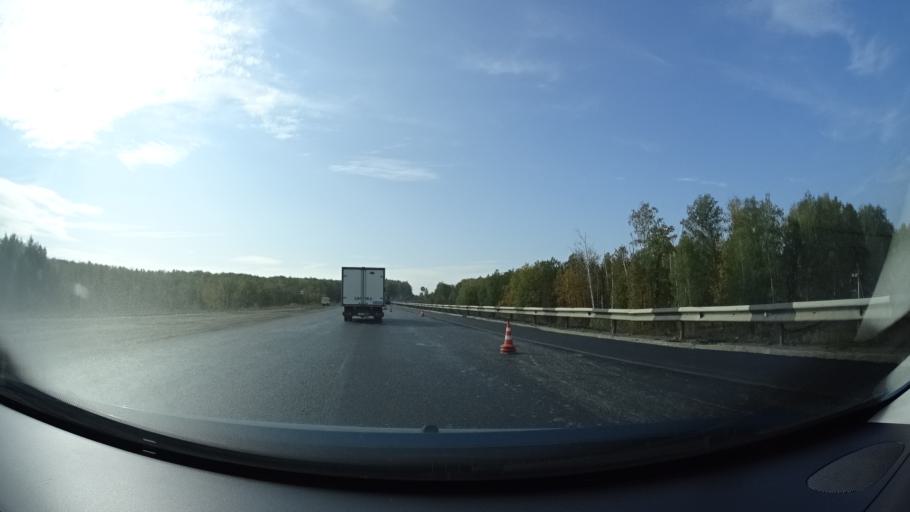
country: RU
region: Bashkortostan
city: Kandry
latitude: 54.5952
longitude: 54.2823
